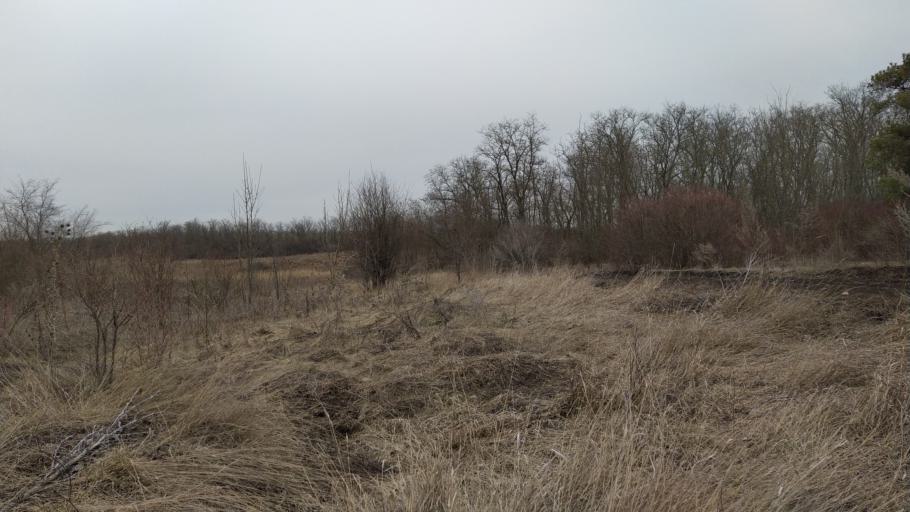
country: RU
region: Rostov
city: Temernik
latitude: 47.3500
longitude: 39.7480
